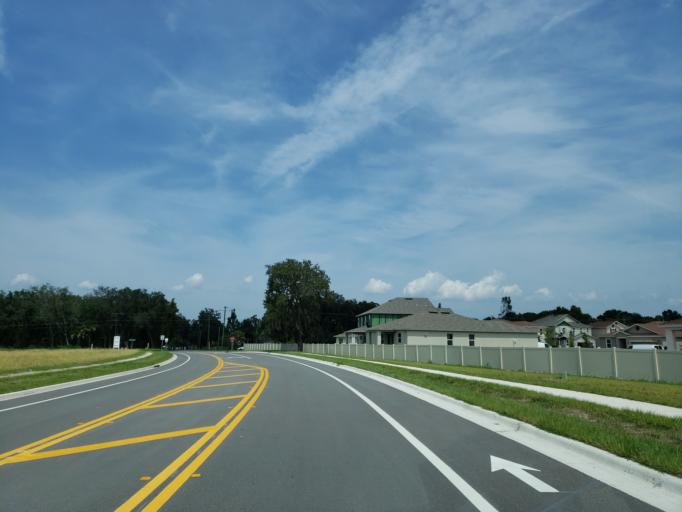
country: US
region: Florida
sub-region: Hillsborough County
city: Riverview
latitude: 27.8450
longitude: -82.3351
